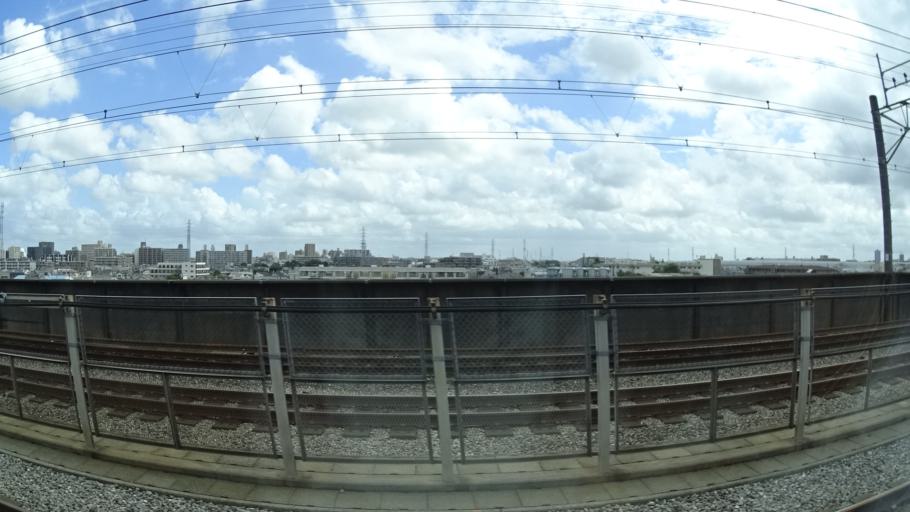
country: JP
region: Saitama
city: Shimotoda
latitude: 35.8380
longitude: 139.6509
